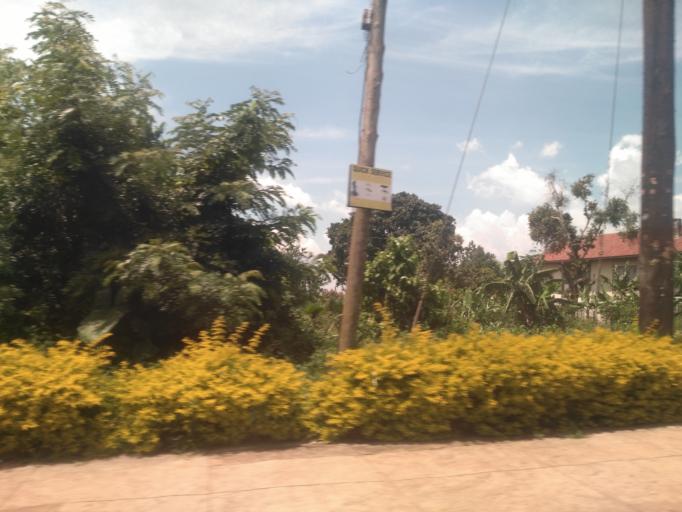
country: UG
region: Central Region
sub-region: Wakiso District
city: Entebbe
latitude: 0.0432
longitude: 32.4621
